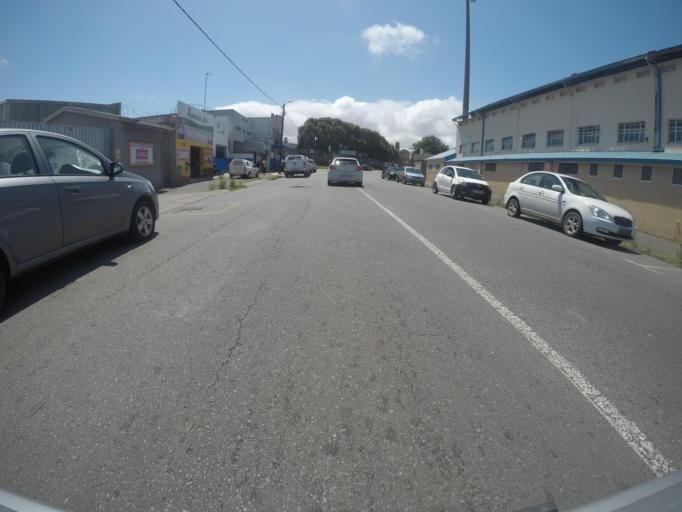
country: ZA
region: Eastern Cape
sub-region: Buffalo City Metropolitan Municipality
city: East London
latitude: -33.0070
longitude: 27.9046
